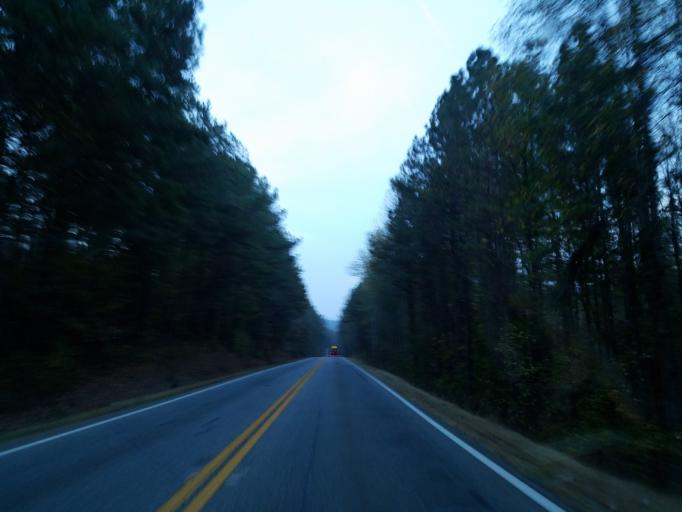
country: US
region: Georgia
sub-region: Pickens County
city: Jasper
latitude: 34.5424
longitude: -84.5825
